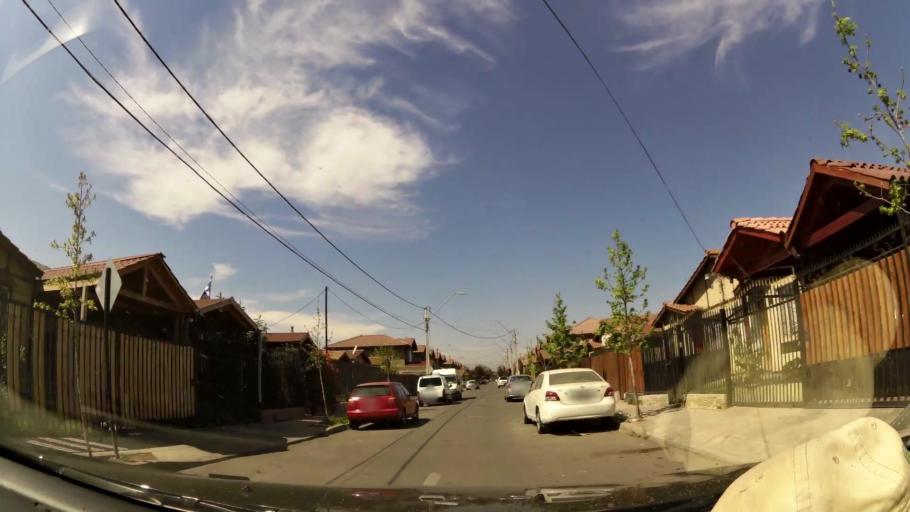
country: CL
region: Santiago Metropolitan
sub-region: Provincia de Santiago
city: Lo Prado
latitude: -33.3940
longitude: -70.7500
